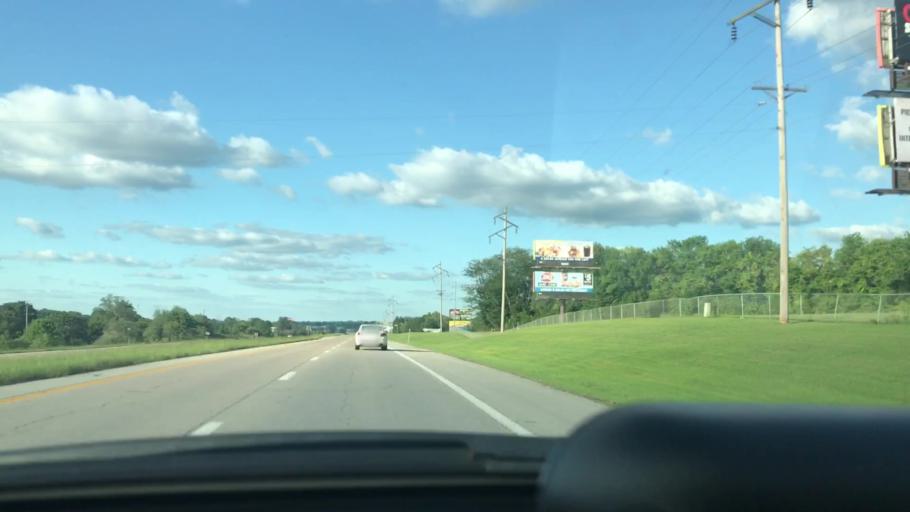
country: US
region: Missouri
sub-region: Pettis County
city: Sedalia
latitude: 38.6423
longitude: -93.2634
